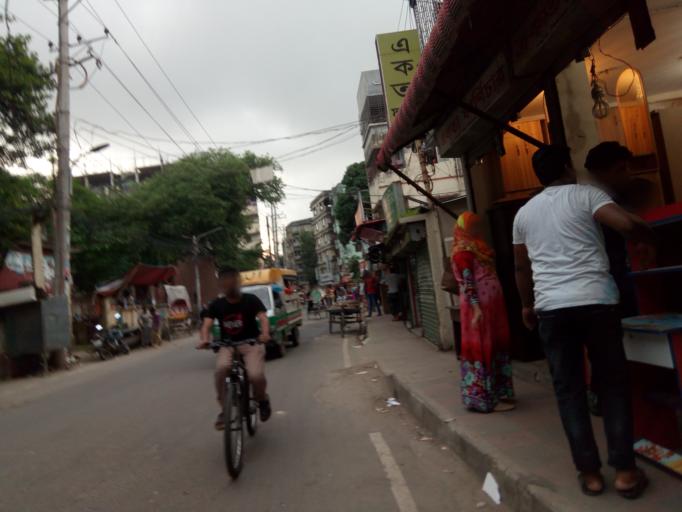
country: BD
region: Dhaka
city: Azimpur
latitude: 23.7264
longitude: 90.3810
